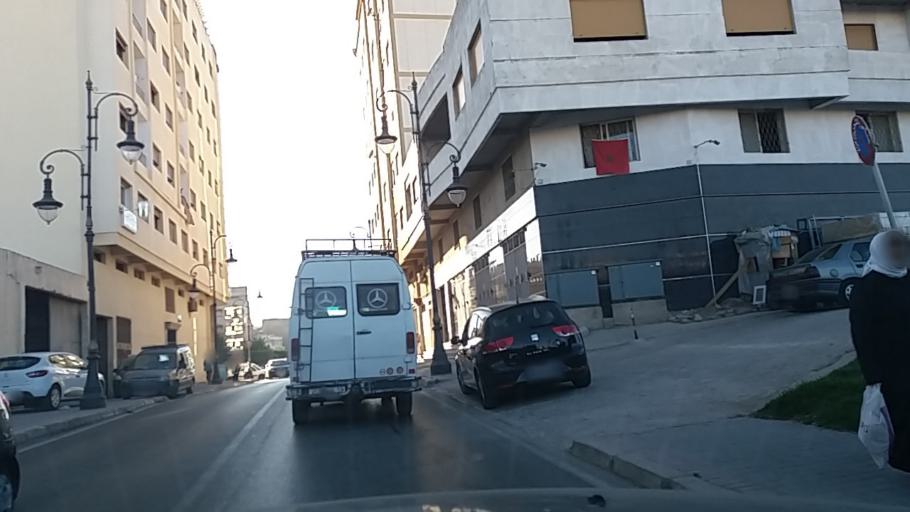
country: MA
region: Tanger-Tetouan
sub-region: Tanger-Assilah
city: Tangier
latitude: 35.7605
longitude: -5.8205
